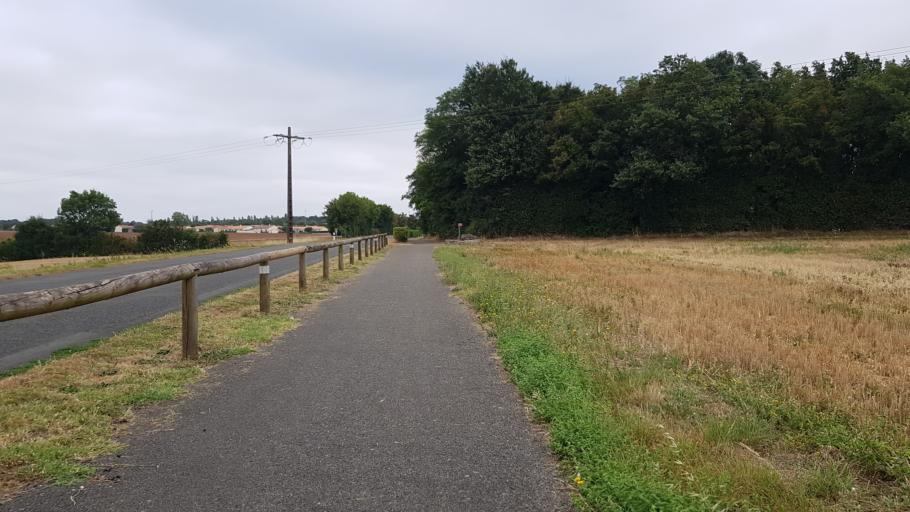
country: FR
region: Poitou-Charentes
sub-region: Departement des Deux-Sevres
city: Vouille
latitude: 46.3207
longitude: -0.3562
